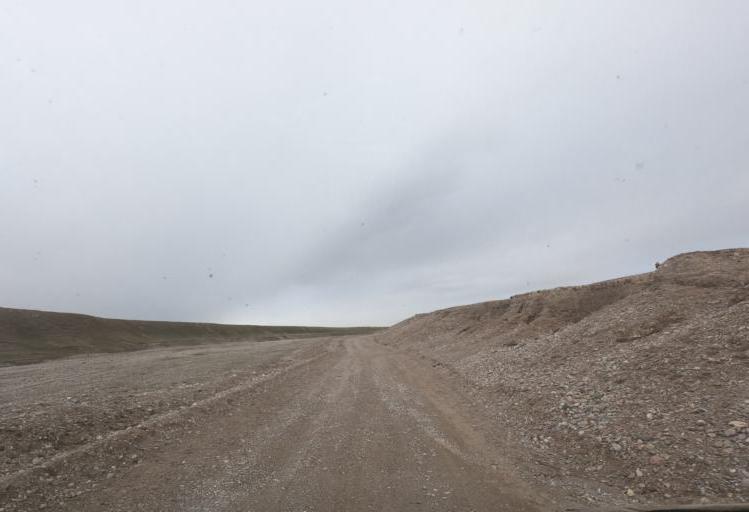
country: KG
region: Naryn
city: Baetov
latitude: 40.9376
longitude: 75.2776
